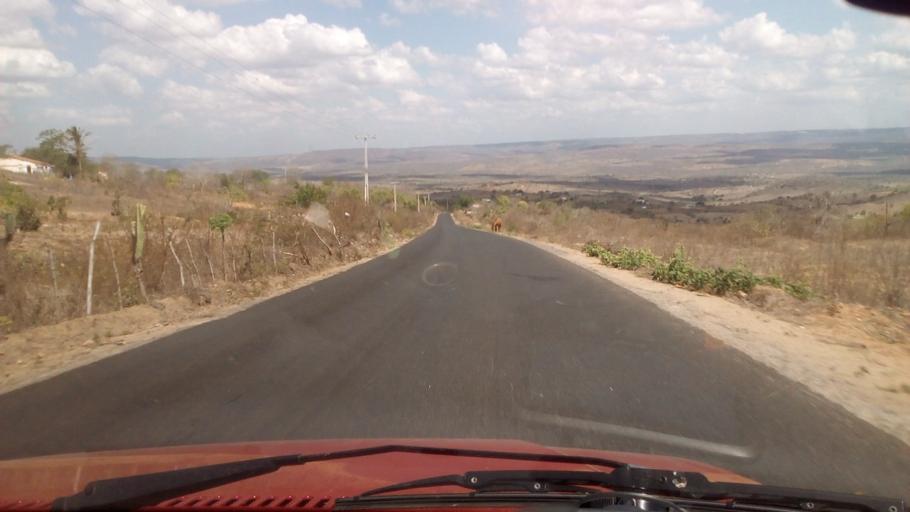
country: BR
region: Paraiba
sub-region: Cacimba De Dentro
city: Cacimba de Dentro
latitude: -6.6498
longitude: -35.7801
